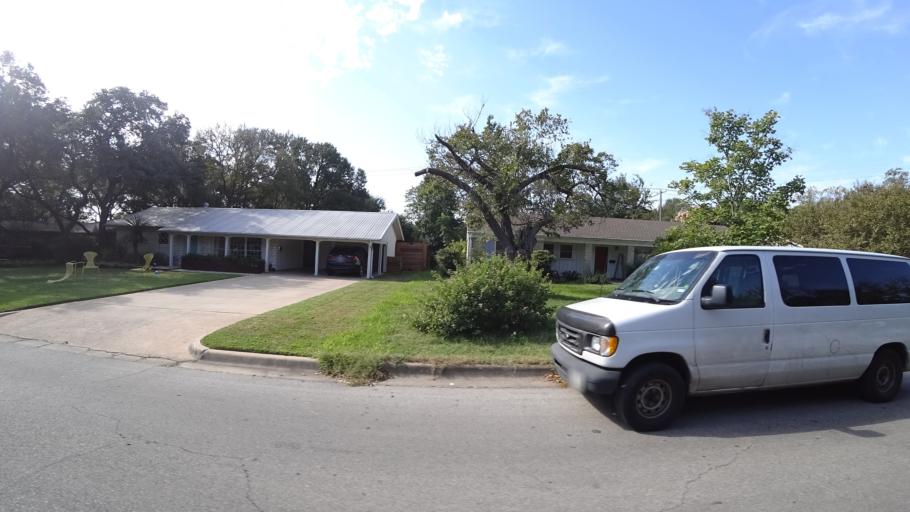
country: US
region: Texas
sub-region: Travis County
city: West Lake Hills
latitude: 30.3391
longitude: -97.7580
